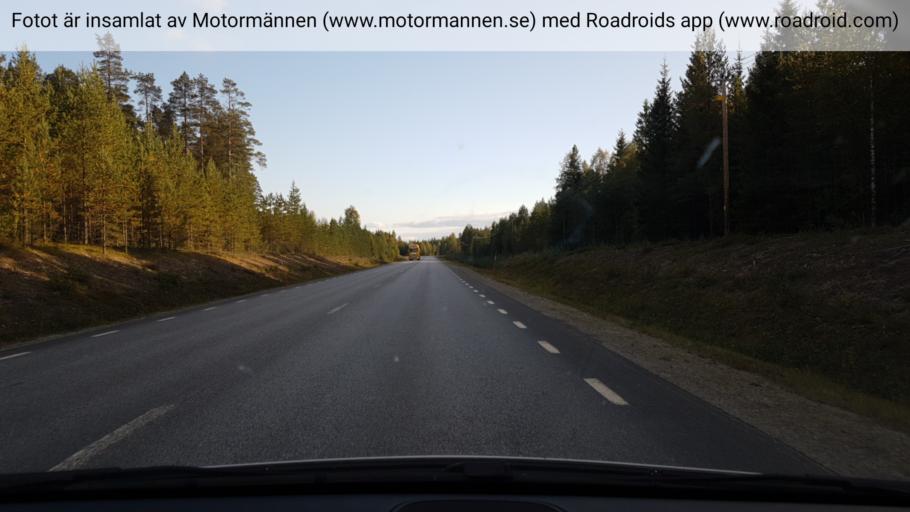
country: SE
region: Vaesterbotten
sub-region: Vannas Kommun
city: Vaennaes
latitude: 64.0170
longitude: 19.6929
